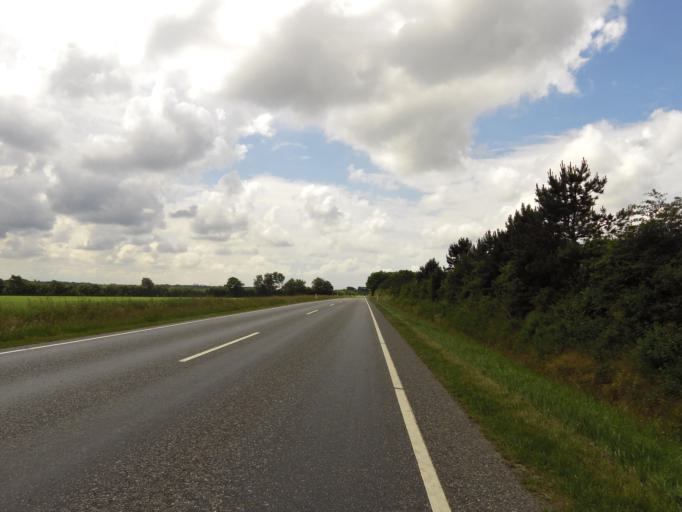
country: DK
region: South Denmark
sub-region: Haderslev Kommune
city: Gram
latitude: 55.2266
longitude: 8.9212
